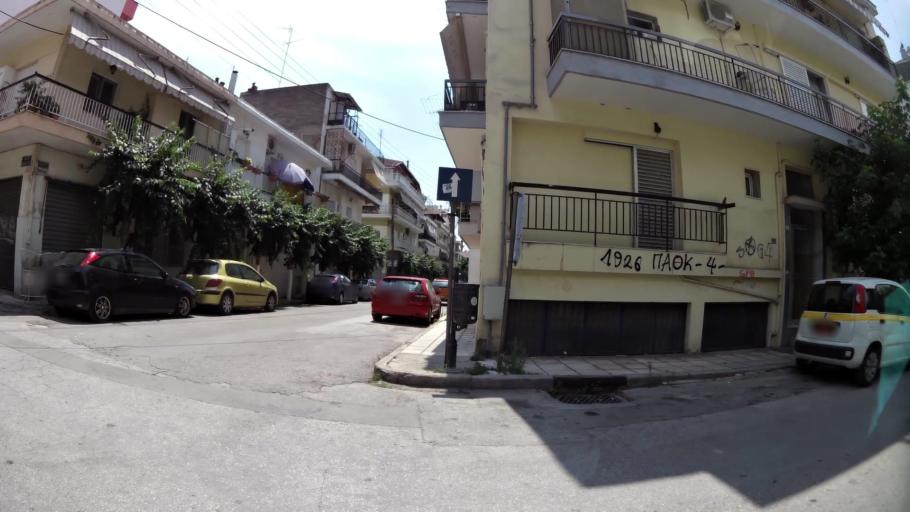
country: GR
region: Central Macedonia
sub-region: Nomos Thessalonikis
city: Ampelokipoi
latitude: 40.6557
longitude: 22.9302
